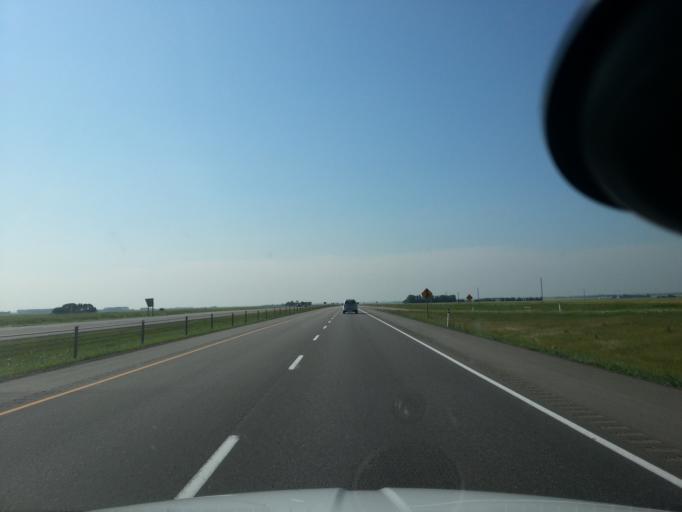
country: CA
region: Alberta
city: Didsbury
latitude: 51.6621
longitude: -114.0256
